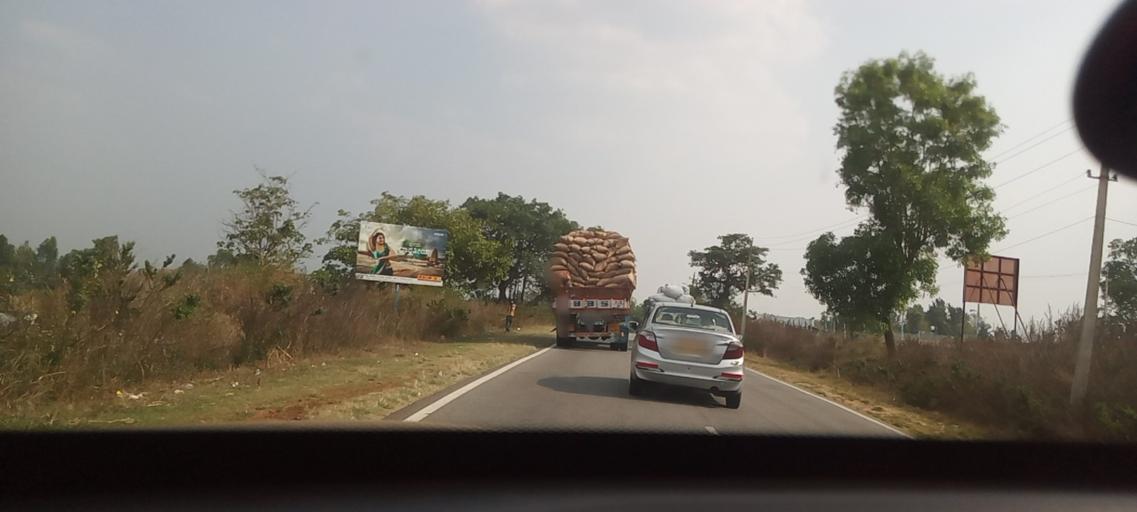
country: IN
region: Karnataka
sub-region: Hassan
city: Hassan
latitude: 13.0733
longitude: 76.0479
